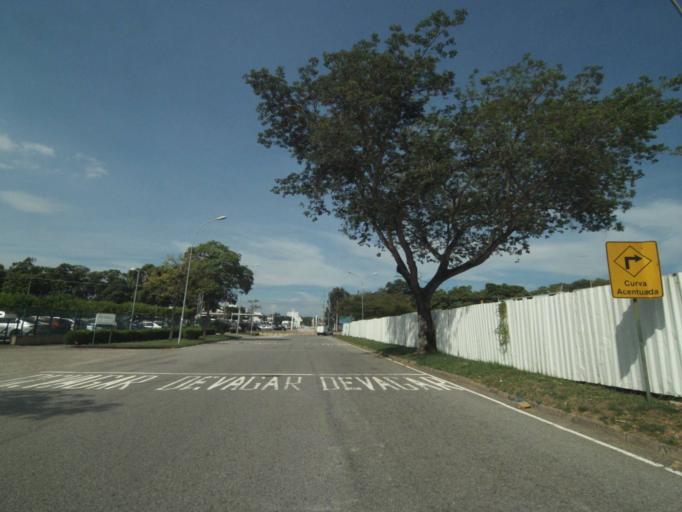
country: BR
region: Rio de Janeiro
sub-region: Rio De Janeiro
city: Rio de Janeiro
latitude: -22.8554
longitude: -43.2325
